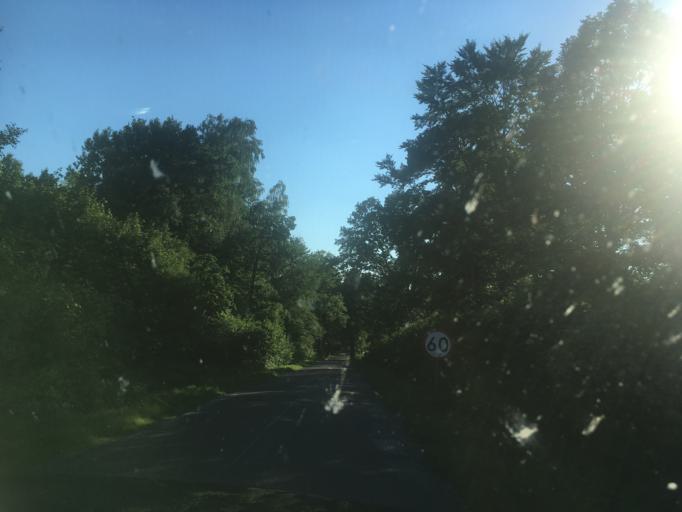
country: PL
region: Warmian-Masurian Voivodeship
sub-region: Powiat ostrodzki
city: Gierzwald
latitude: 53.6263
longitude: 20.0470
